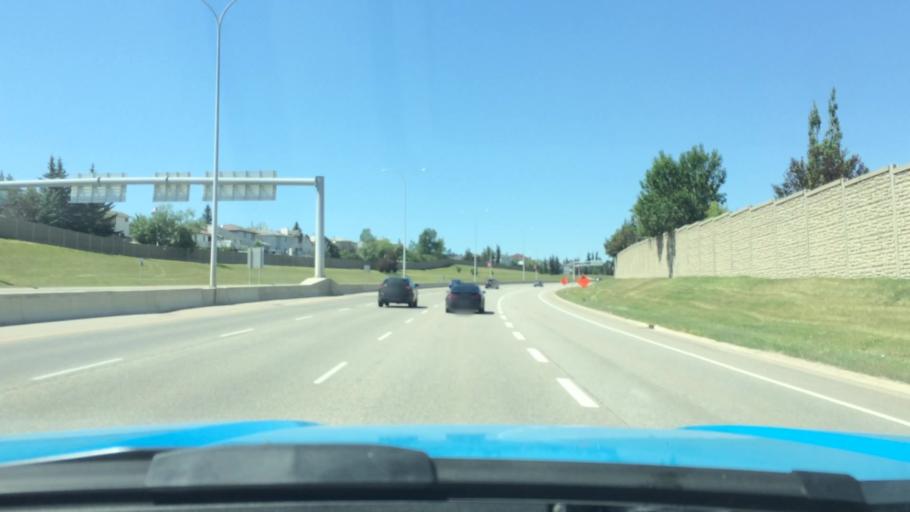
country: CA
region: Alberta
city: Calgary
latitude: 51.1428
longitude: -114.0981
